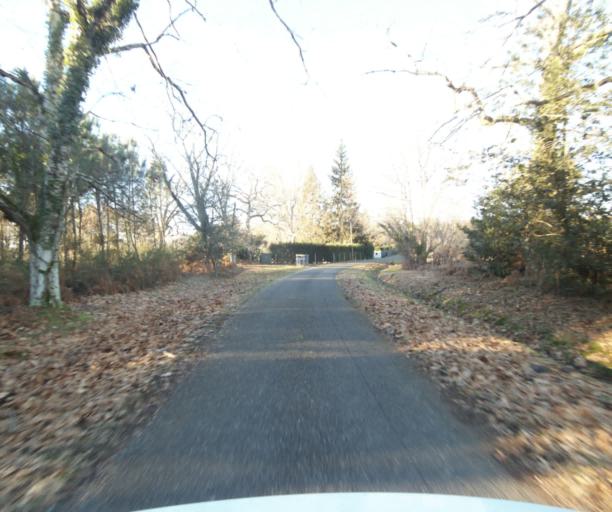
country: FR
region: Aquitaine
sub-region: Departement des Landes
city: Sarbazan
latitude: 44.1055
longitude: -0.1458
